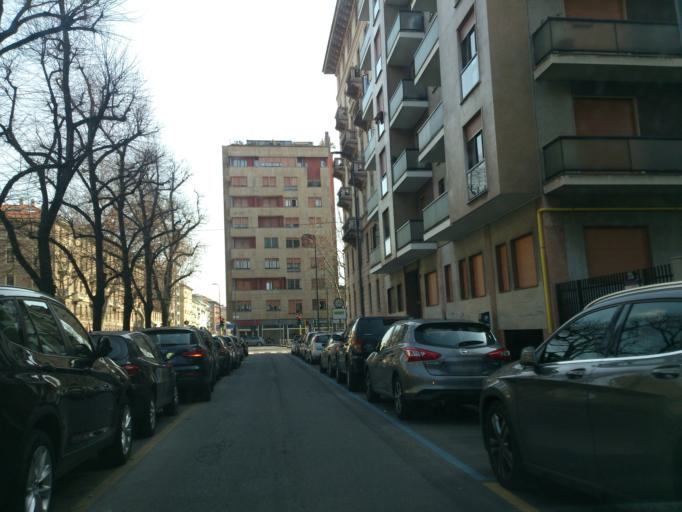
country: IT
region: Lombardy
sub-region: Citta metropolitana di Milano
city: Milano
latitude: 45.4529
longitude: 9.2134
